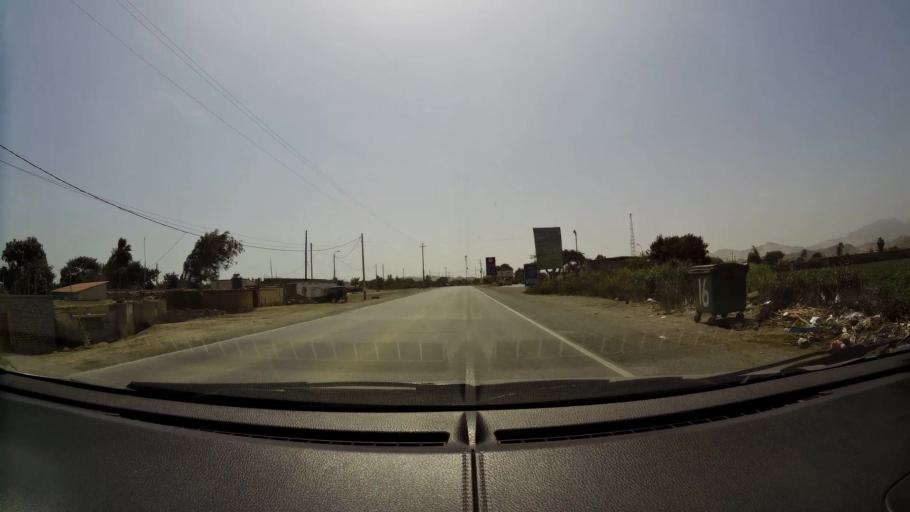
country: PE
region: Ancash
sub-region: Provincia de Huarmey
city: Huarmey
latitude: -10.0750
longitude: -78.1536
